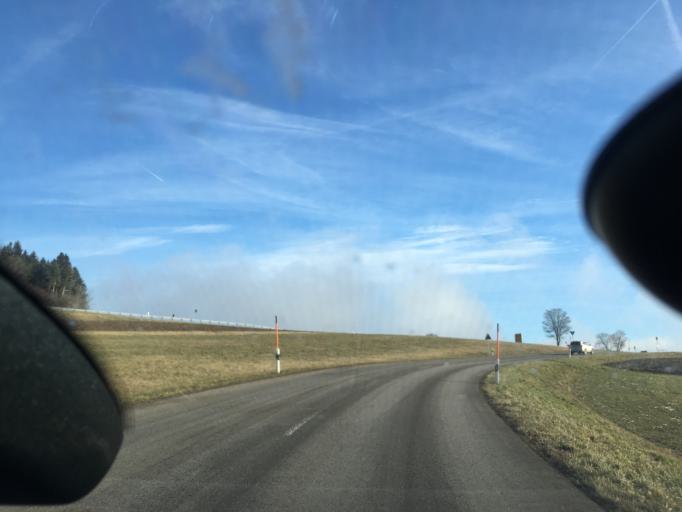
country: DE
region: Baden-Wuerttemberg
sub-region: Freiburg Region
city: Dogern
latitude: 47.6630
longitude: 8.1614
